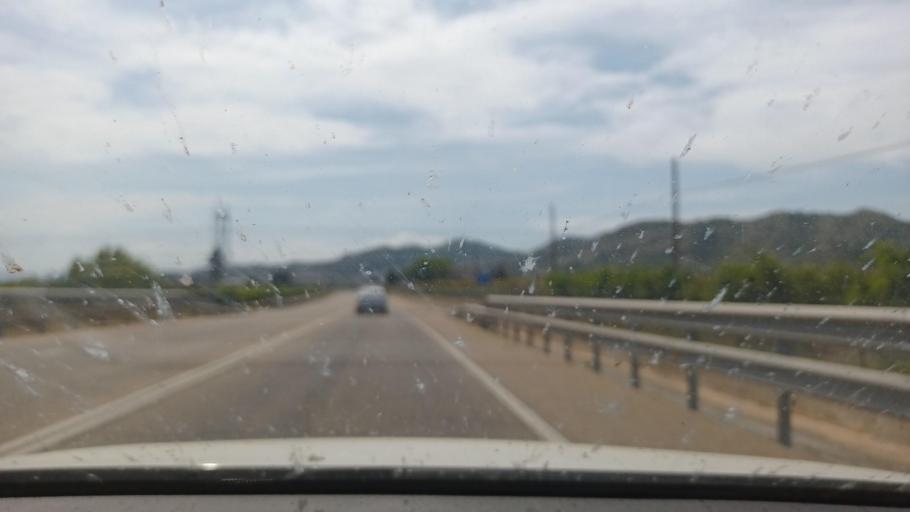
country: ES
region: Valencia
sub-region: Provincia de Castello
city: Castello de la Plana
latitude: 40.0244
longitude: -0.0212
